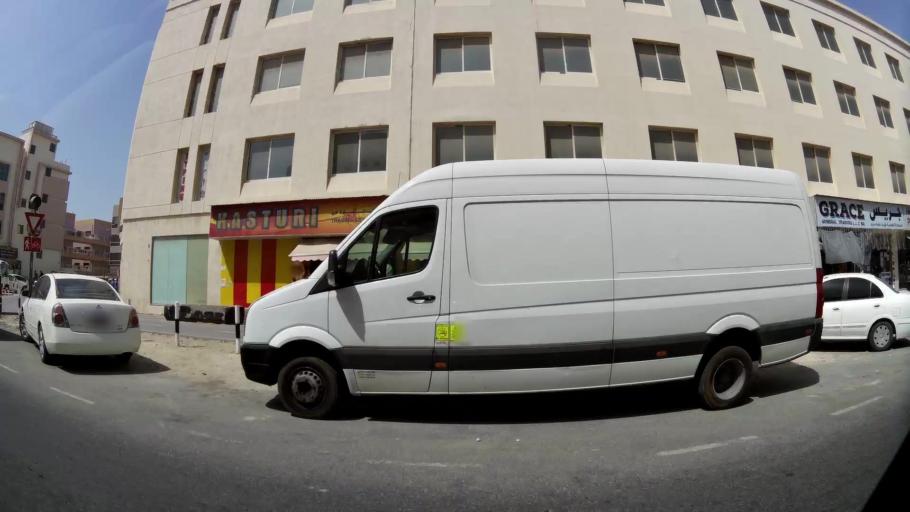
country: AE
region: Dubai
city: Dubai
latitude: 25.1581
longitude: 55.2493
